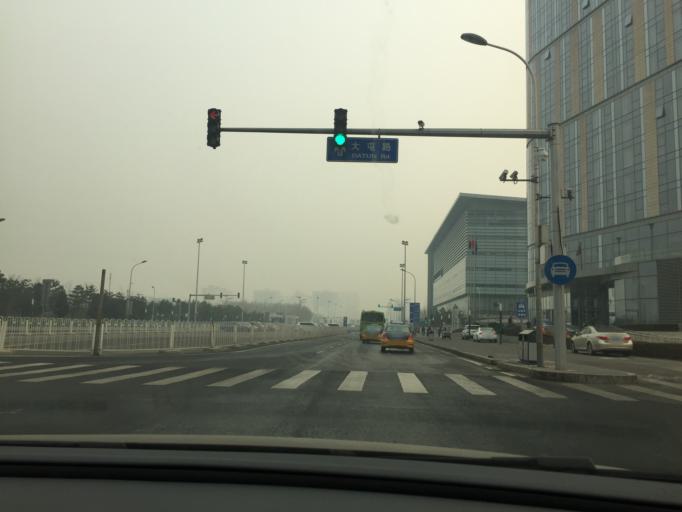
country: CN
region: Beijing
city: Datun
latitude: 40.0005
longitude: 116.3808
